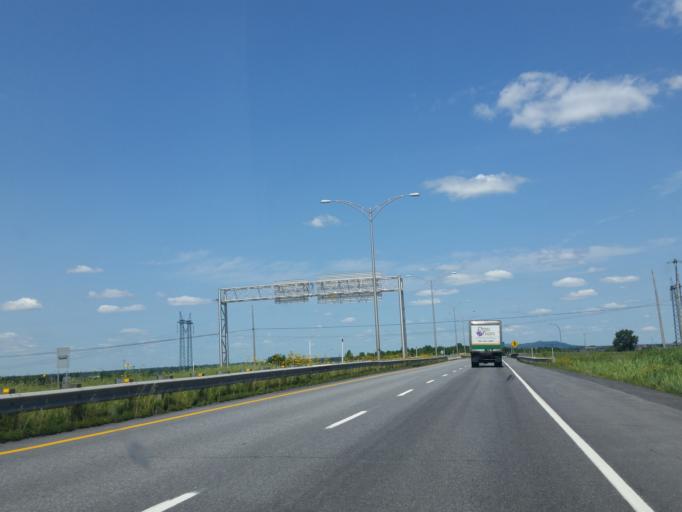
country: CA
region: Quebec
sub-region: Monteregie
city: Carignan
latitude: 45.4061
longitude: -73.3149
